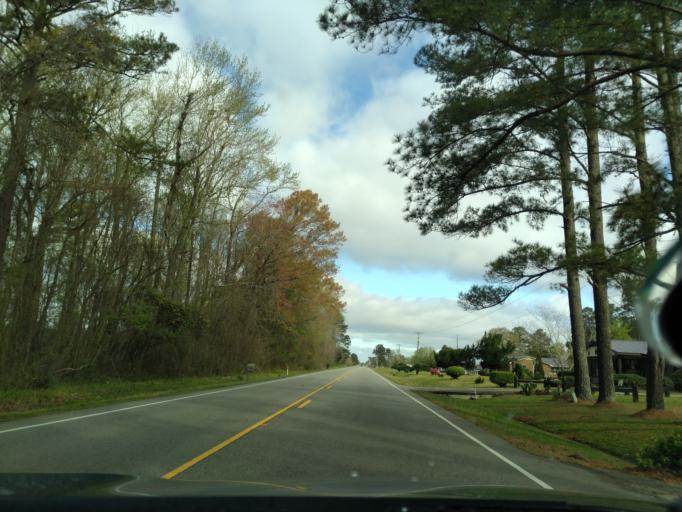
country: US
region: North Carolina
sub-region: Washington County
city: Plymouth
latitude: 35.8854
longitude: -76.6976
